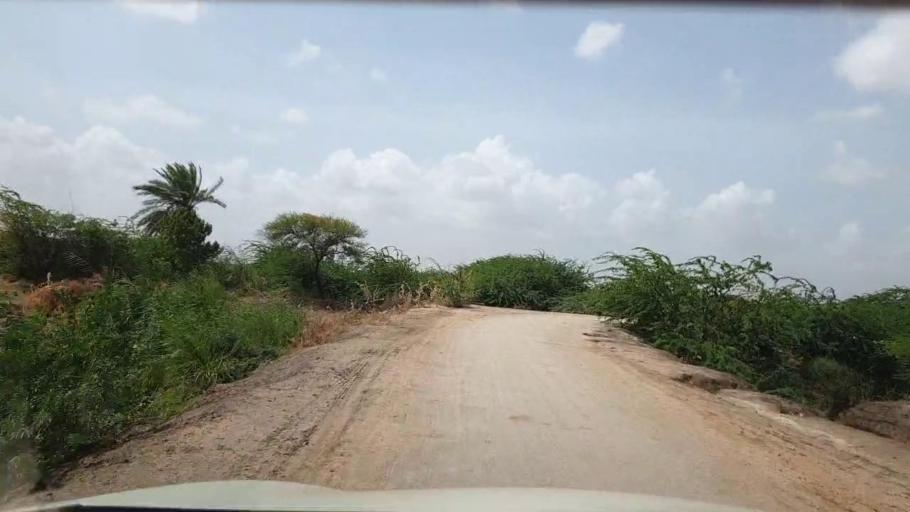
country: PK
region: Sindh
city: Kadhan
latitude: 24.4224
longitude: 68.8322
